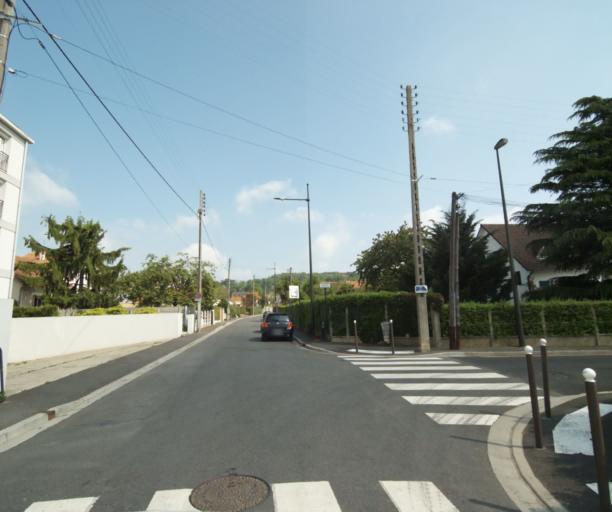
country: FR
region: Ile-de-France
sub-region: Departement du Val-d'Oise
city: Franconville
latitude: 48.9617
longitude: 2.2278
